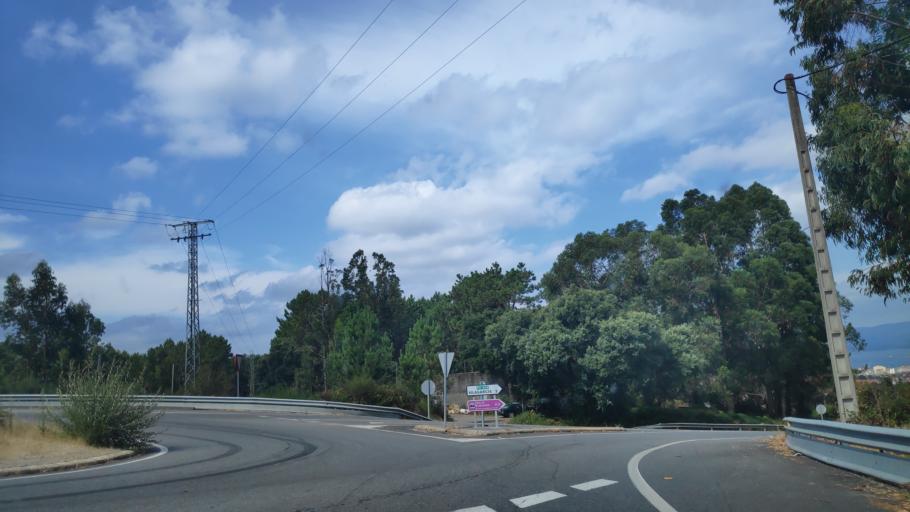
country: ES
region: Galicia
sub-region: Provincia de Pontevedra
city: Vilagarcia de Arousa
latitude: 42.5934
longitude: -8.7300
